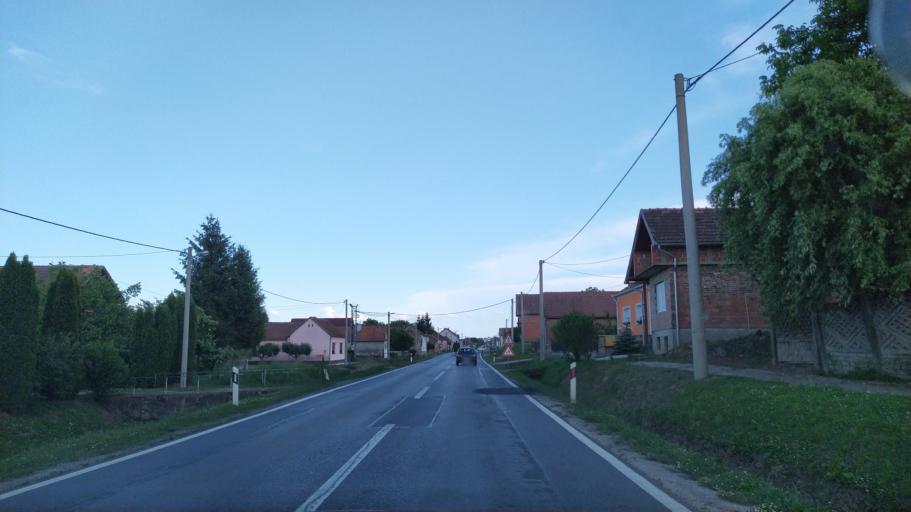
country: HR
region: Virovitick-Podravska
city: Slatina
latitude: 45.7324
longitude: 17.6234
